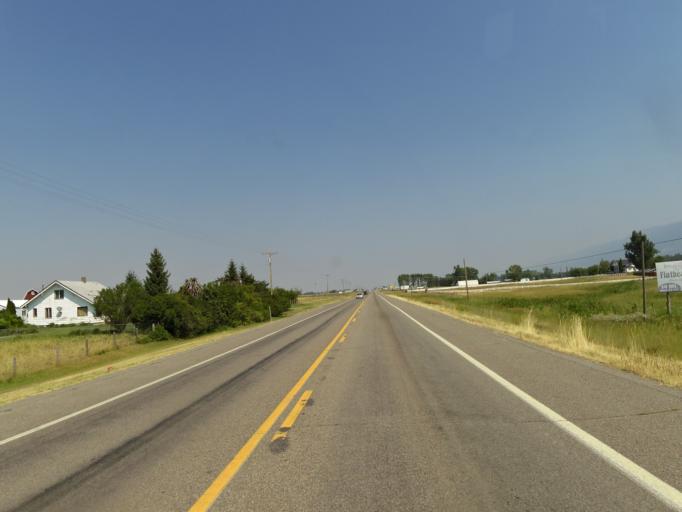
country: US
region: Montana
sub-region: Lake County
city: Ronan
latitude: 47.5012
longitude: -114.0970
